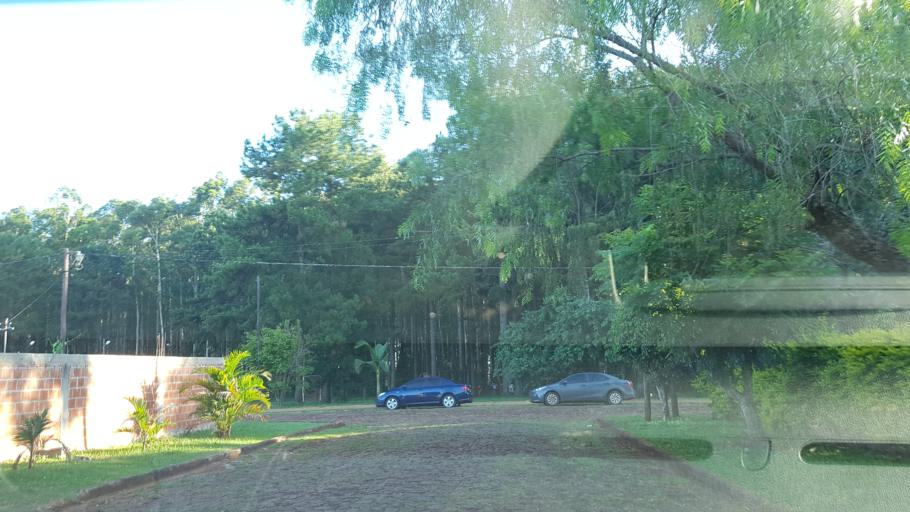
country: AR
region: Misiones
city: Puerto Libertad
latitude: -25.9245
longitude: -54.5850
